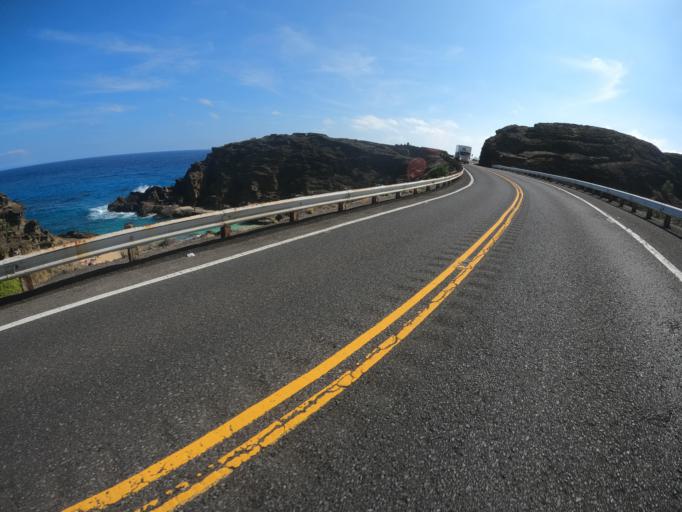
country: US
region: Hawaii
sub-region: Honolulu County
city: Waimanalo Beach
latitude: 21.2822
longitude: -157.6778
